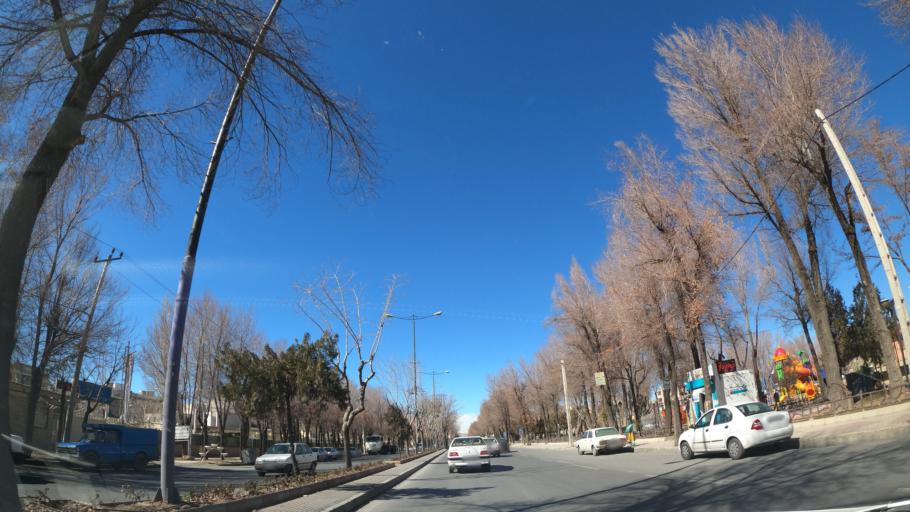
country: IR
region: Chahar Mahall va Bakhtiari
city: Shahrekord
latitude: 32.3121
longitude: 50.8827
